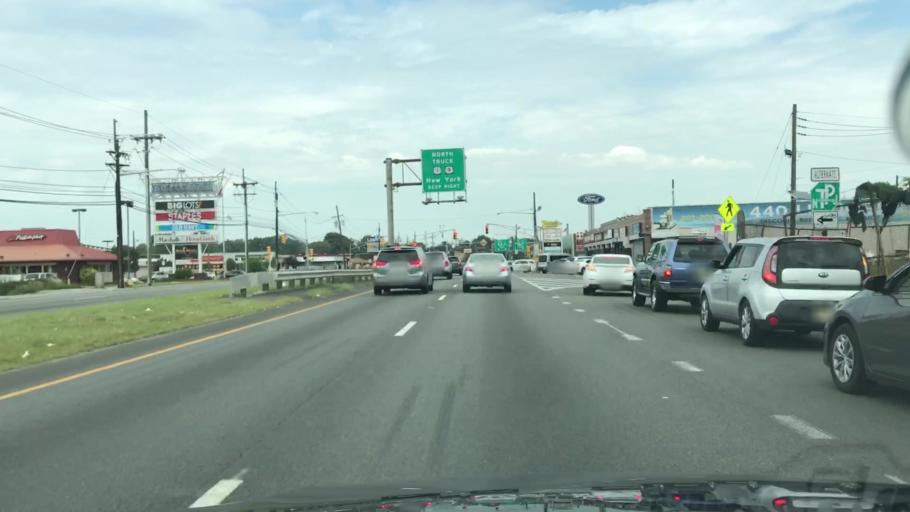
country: US
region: New Jersey
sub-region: Hudson County
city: Jersey City
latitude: 40.7197
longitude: -74.0933
